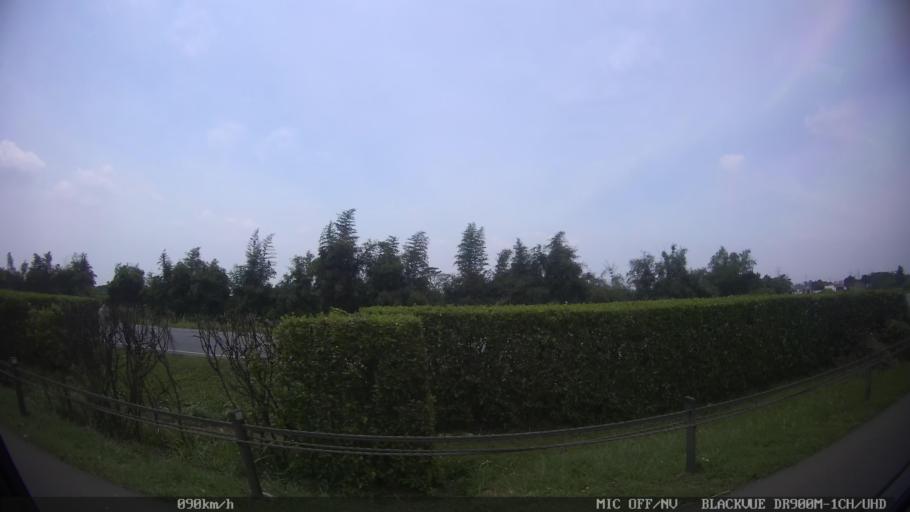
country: ID
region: West Java
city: Kresek
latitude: -6.1585
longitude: 106.3263
